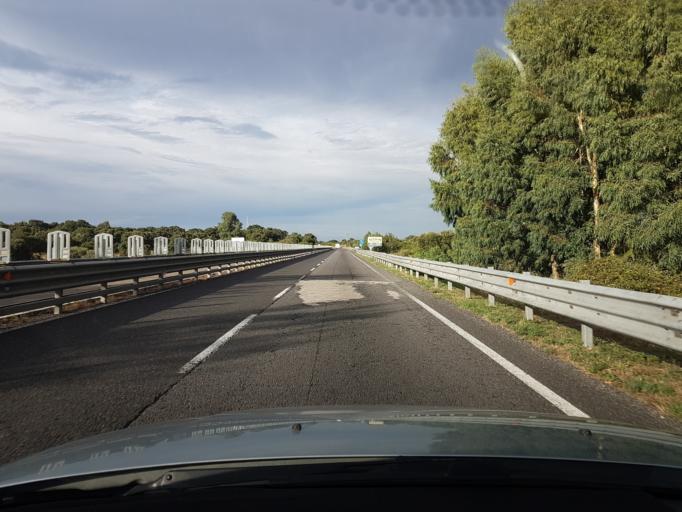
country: IT
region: Sardinia
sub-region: Provincia di Oristano
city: Paulilatino
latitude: 40.0999
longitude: 8.7822
